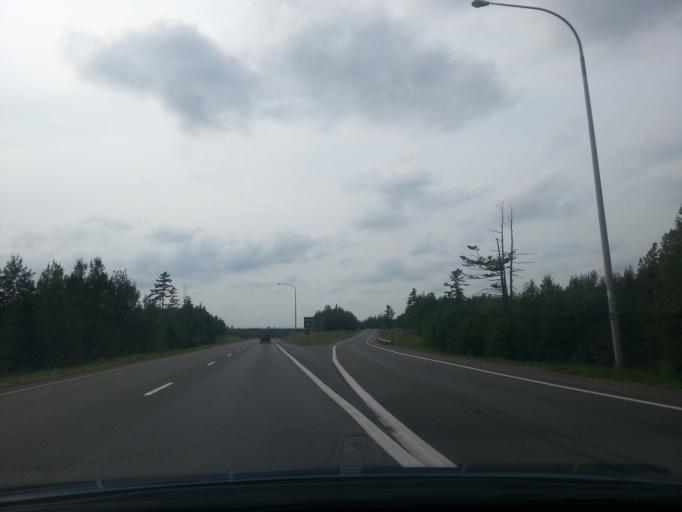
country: CA
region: New Brunswick
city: Oromocto
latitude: 45.8522
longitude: -66.5563
